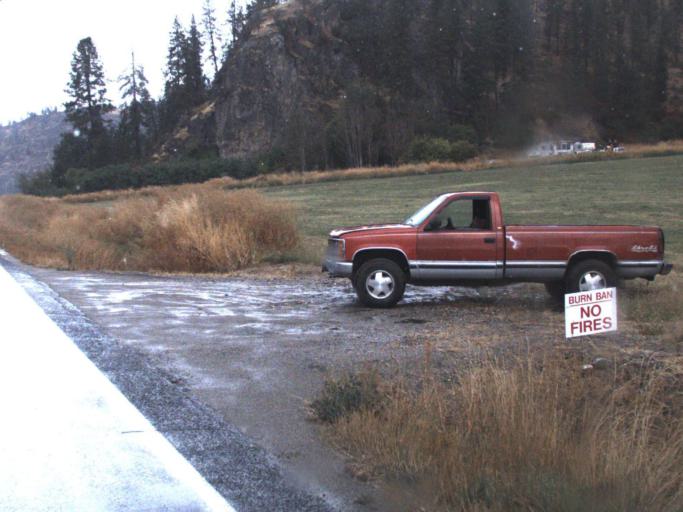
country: US
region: Washington
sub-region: Stevens County
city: Chewelah
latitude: 48.1780
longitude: -117.7282
